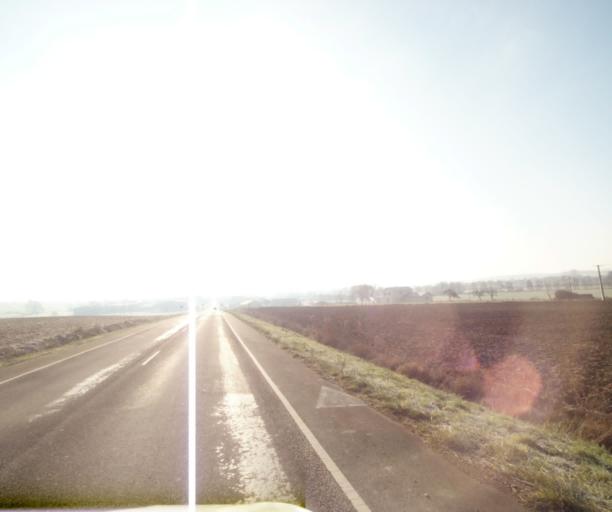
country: FR
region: Champagne-Ardenne
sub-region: Departement de la Haute-Marne
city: Montier-en-Der
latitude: 48.4911
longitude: 4.7569
